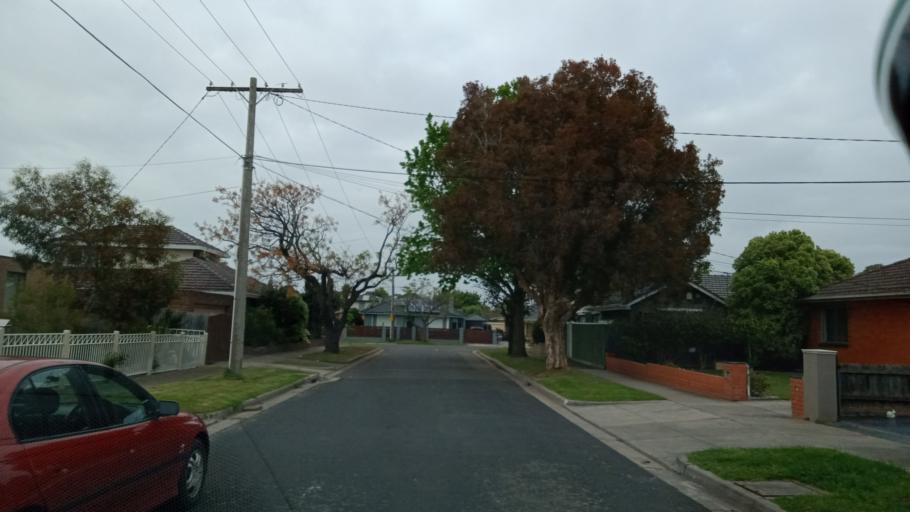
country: AU
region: Victoria
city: McKinnon
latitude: -37.9310
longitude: 145.0640
